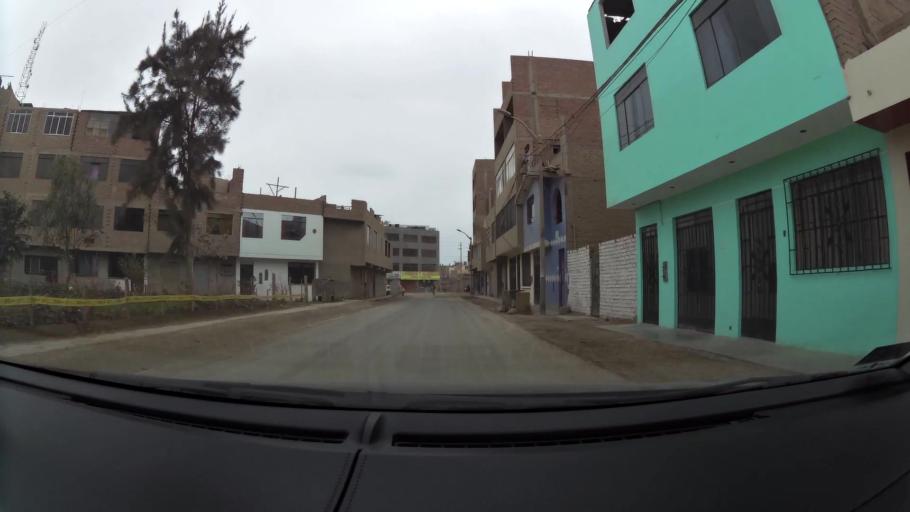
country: PE
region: Lima
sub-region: Lima
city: Independencia
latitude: -11.9720
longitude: -77.0927
